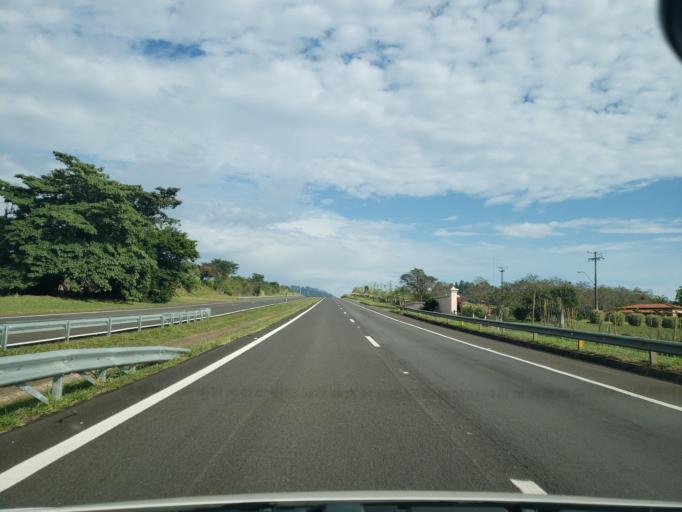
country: BR
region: Sao Paulo
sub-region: Dois Corregos
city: Dois Corregos
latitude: -22.2440
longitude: -48.3138
